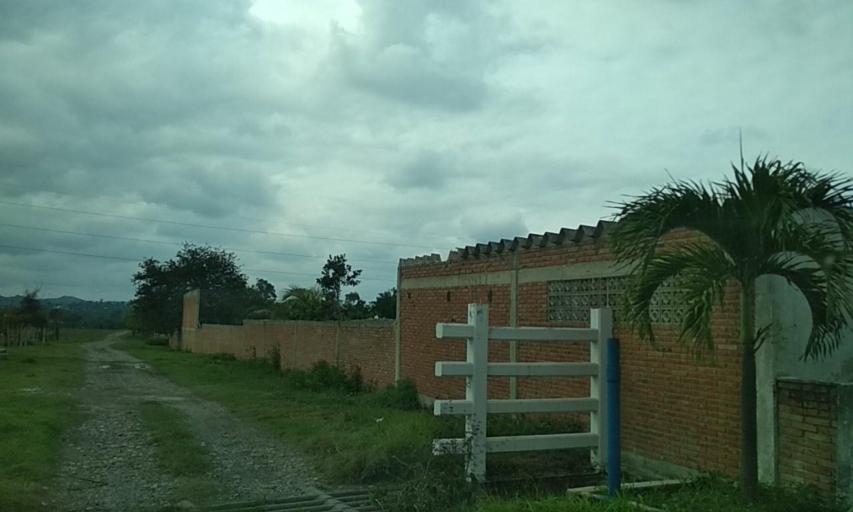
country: MX
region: Veracruz
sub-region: Papantla
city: El Chote
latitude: 20.3925
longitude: -97.3365
